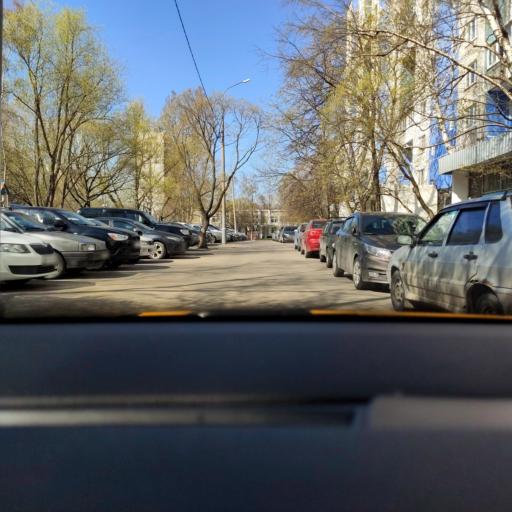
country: RU
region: Moskovskaya
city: Vostochnoe Degunino
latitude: 55.8899
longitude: 37.5627
